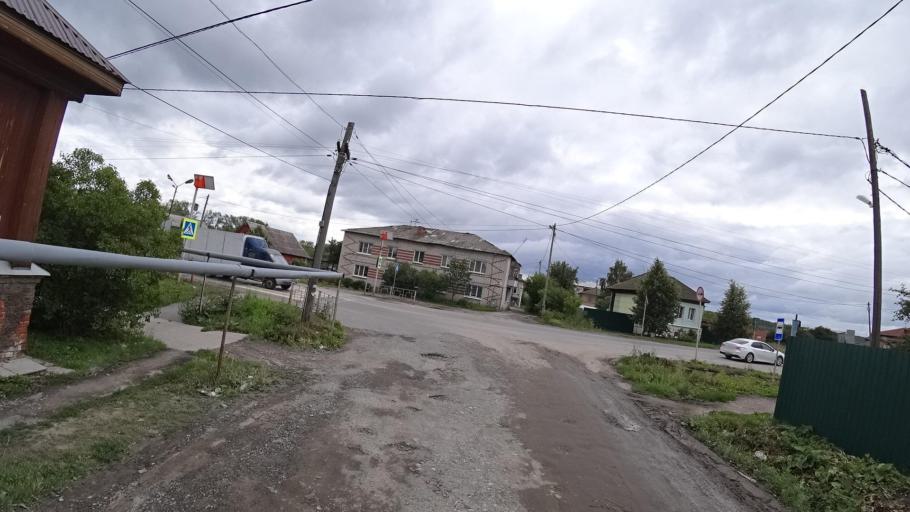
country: RU
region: Sverdlovsk
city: Kamyshlov
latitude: 56.8468
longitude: 62.6815
